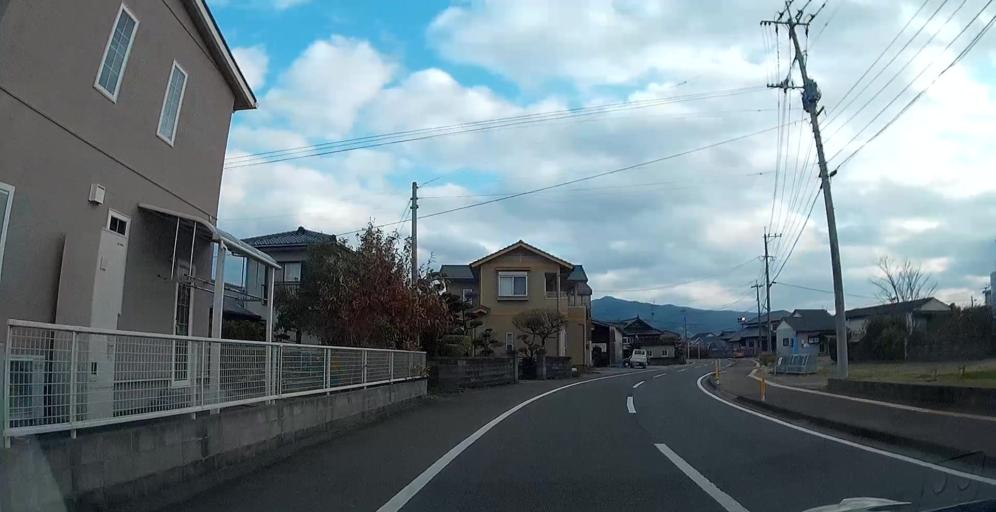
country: JP
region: Kumamoto
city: Yatsushiro
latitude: 32.5346
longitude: 130.6354
